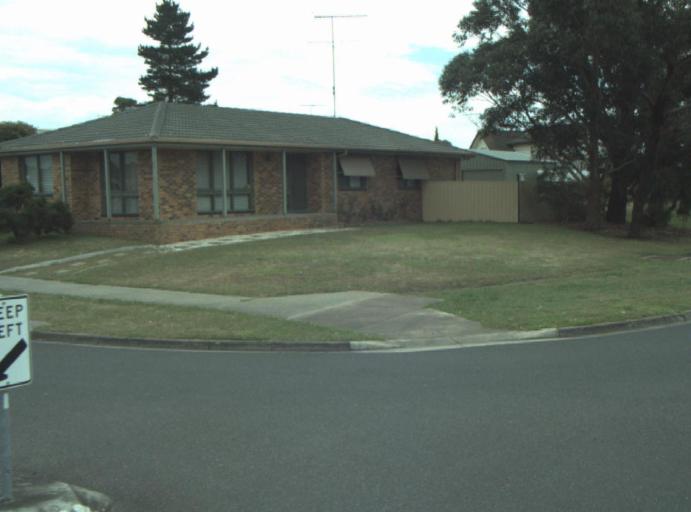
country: AU
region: Victoria
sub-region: Greater Geelong
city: Breakwater
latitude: -38.1861
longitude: 144.4002
